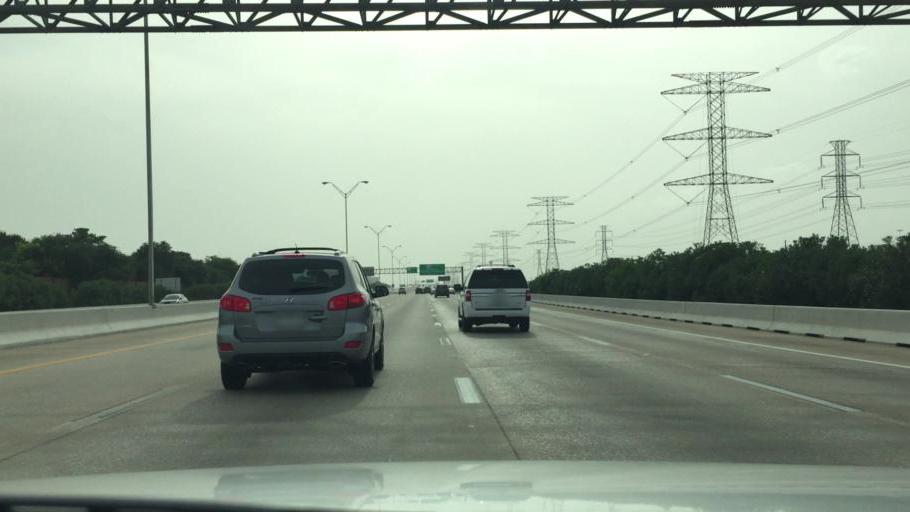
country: US
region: Texas
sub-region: Harris County
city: Hudson
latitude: 29.9376
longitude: -95.4876
